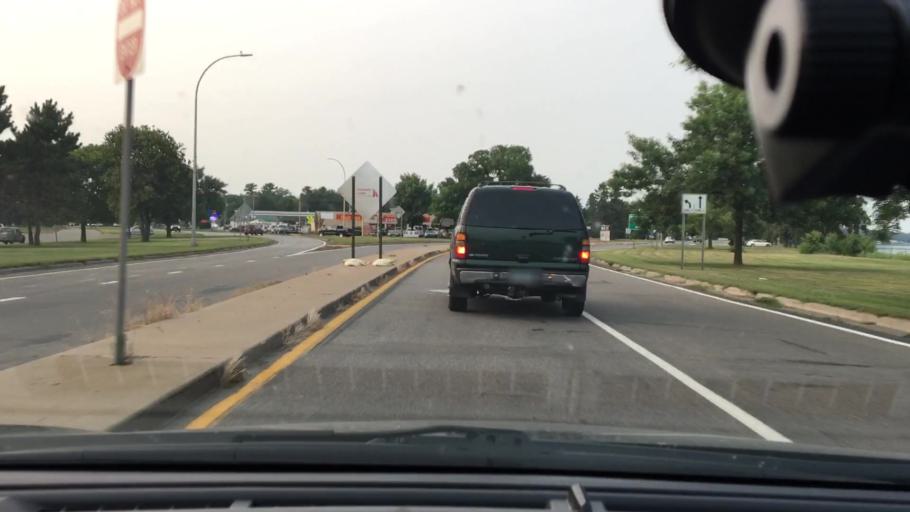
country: US
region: Minnesota
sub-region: Mille Lacs County
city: Vineland
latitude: 46.2943
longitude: -93.8245
